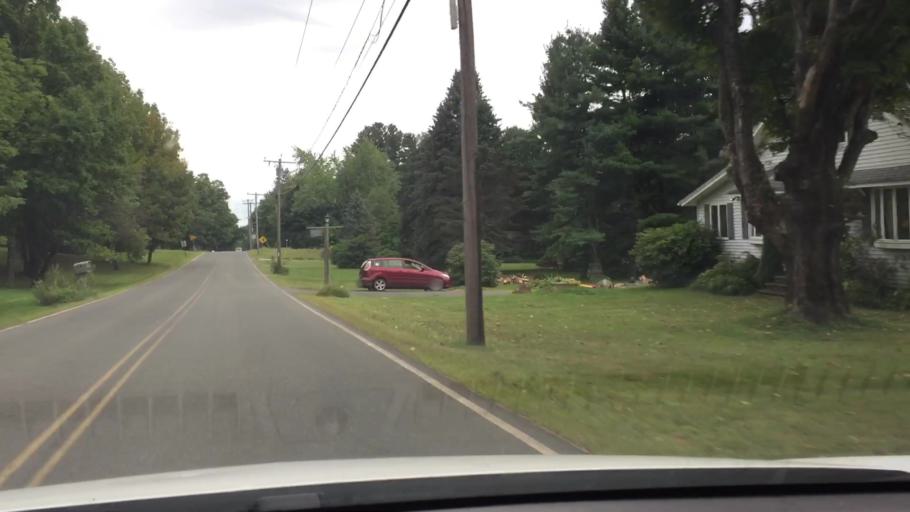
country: US
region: Massachusetts
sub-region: Berkshire County
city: Otis
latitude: 42.2045
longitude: -72.9399
